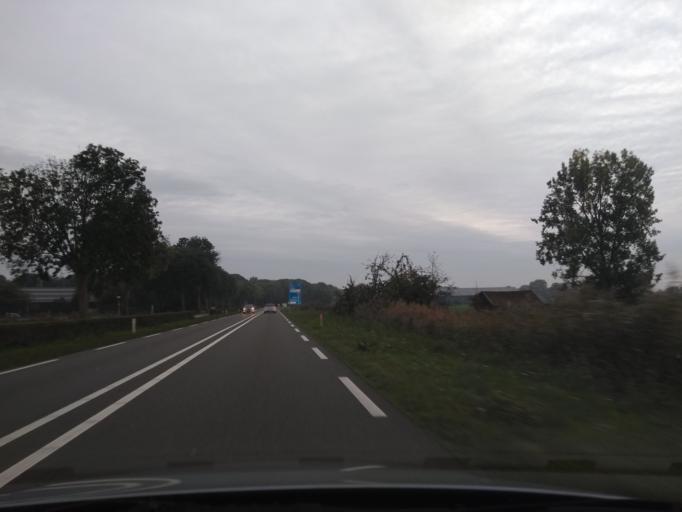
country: NL
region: Overijssel
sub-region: Gemeente Zwartewaterland
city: Hasselt
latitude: 52.5994
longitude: 6.0968
